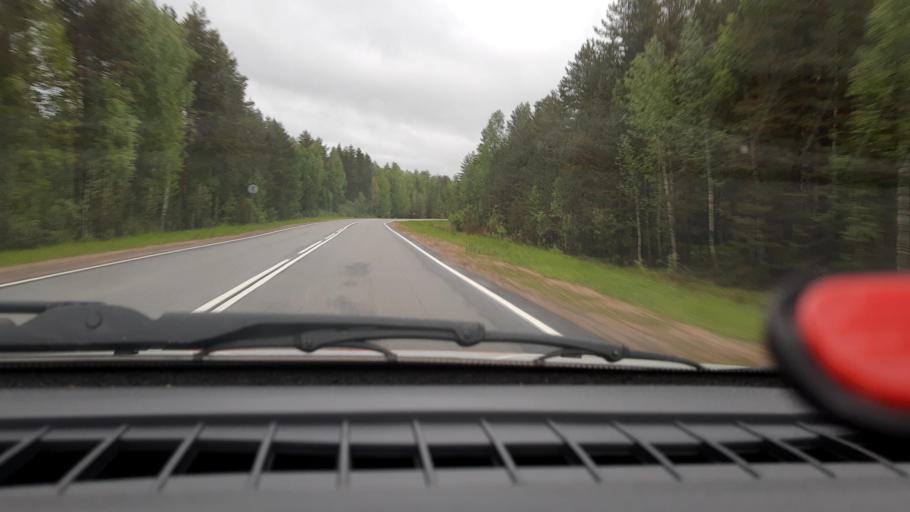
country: RU
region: Nizjnij Novgorod
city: Krasnyye Baki
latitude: 57.2102
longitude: 45.4621
